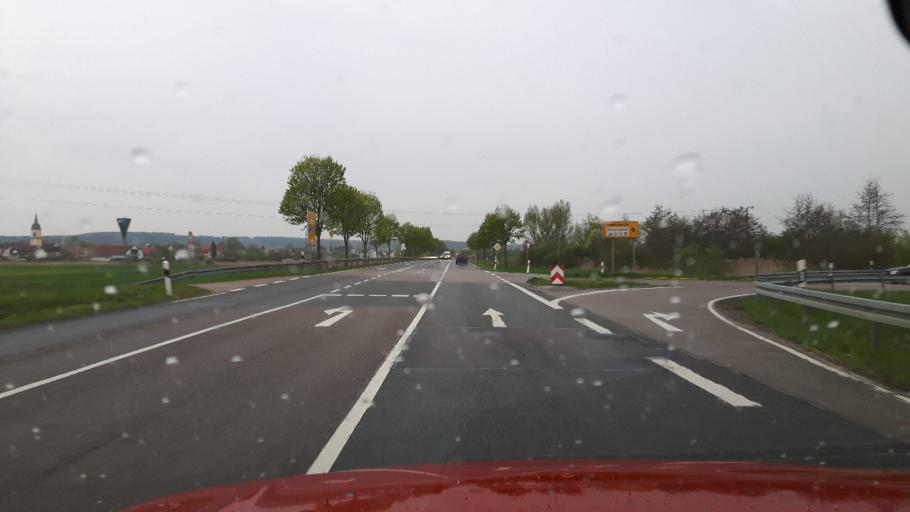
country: DE
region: Bavaria
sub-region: Regierungsbezirk Mittelfranken
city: Gunzenhausen
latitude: 49.1014
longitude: 10.7584
